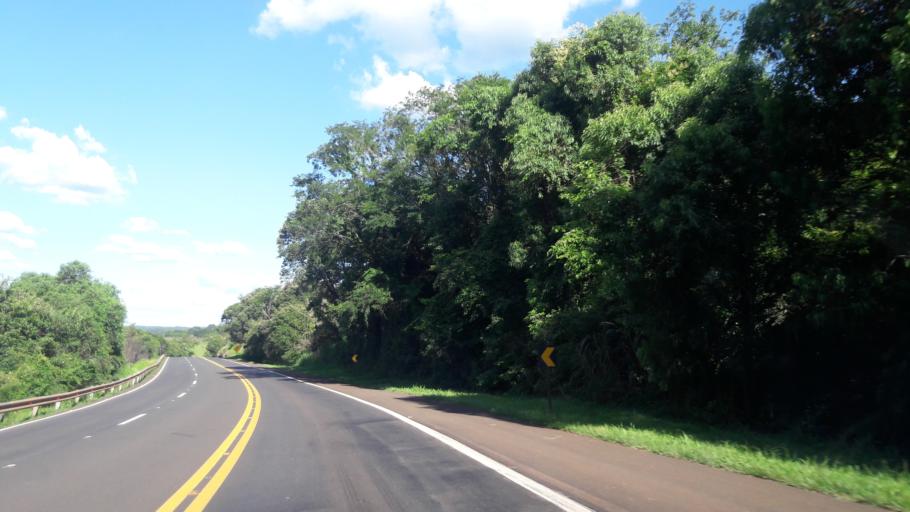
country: BR
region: Parana
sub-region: Laranjeiras Do Sul
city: Laranjeiras do Sul
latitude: -25.4053
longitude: -52.0974
